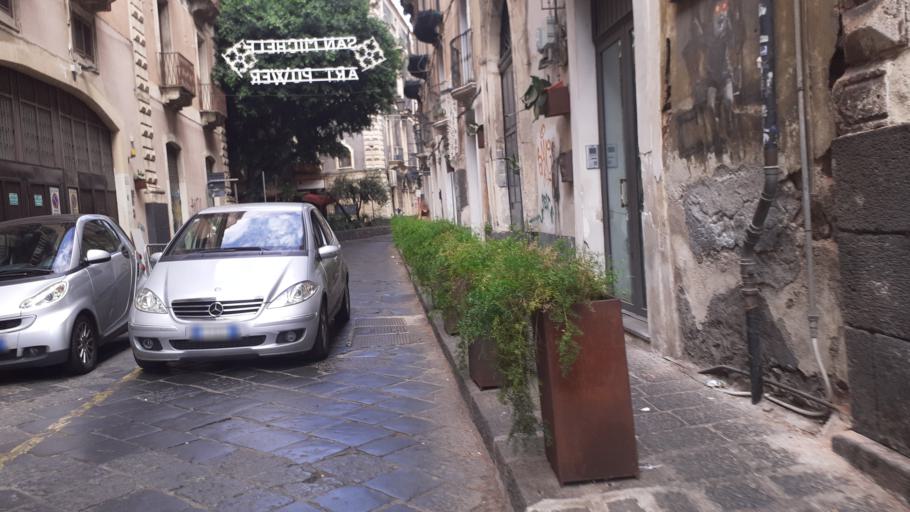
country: IT
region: Sicily
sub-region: Catania
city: Catania
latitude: 37.5061
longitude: 15.0875
